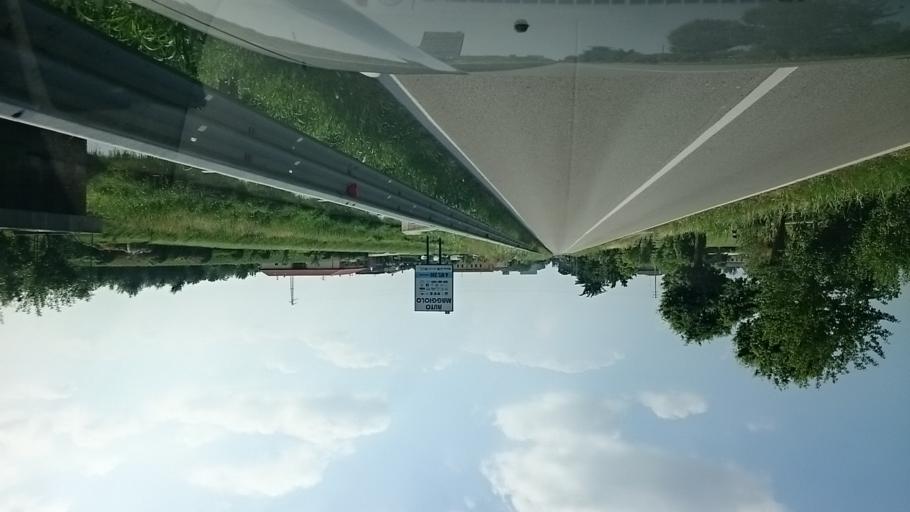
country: IT
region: Veneto
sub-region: Provincia di Padova
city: Cavino
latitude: 45.5259
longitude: 11.8688
